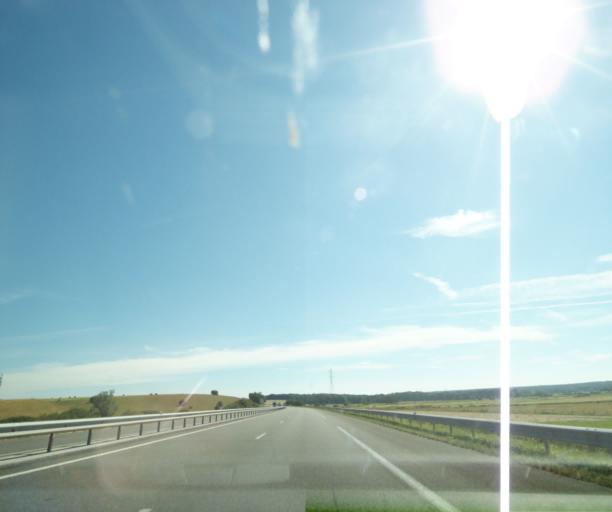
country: FR
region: Lorraine
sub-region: Departement des Vosges
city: Bulgneville
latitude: 48.1931
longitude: 5.7750
